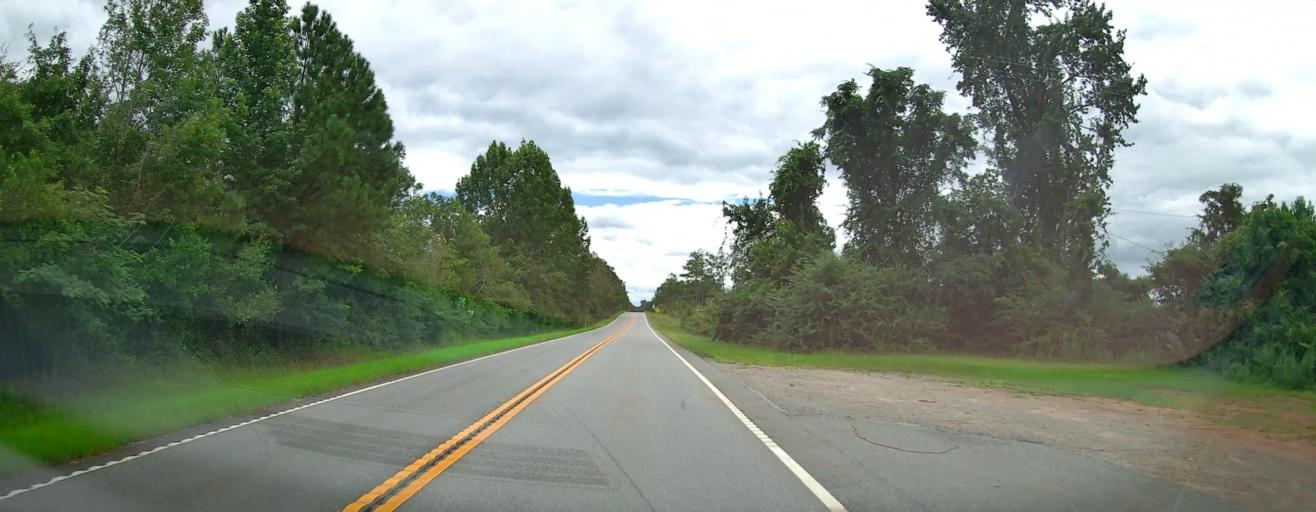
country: US
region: Georgia
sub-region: Twiggs County
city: Jeffersonville
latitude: 32.6706
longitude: -83.3279
